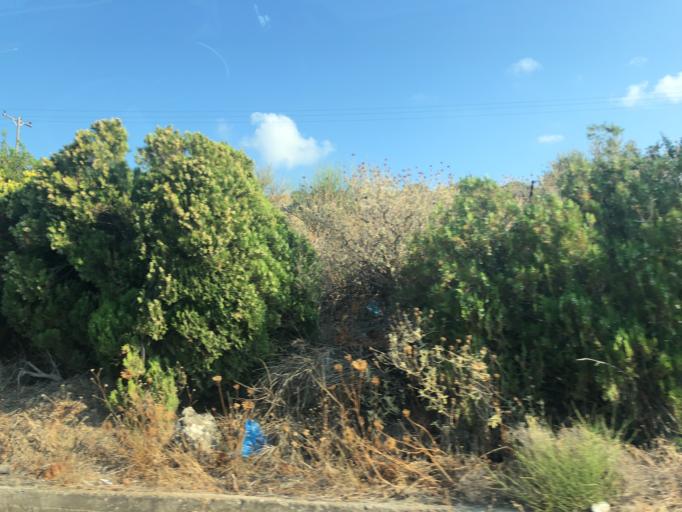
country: GR
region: Crete
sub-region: Nomos Rethymnis
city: Atsipopoulon
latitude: 35.3663
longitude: 24.4324
